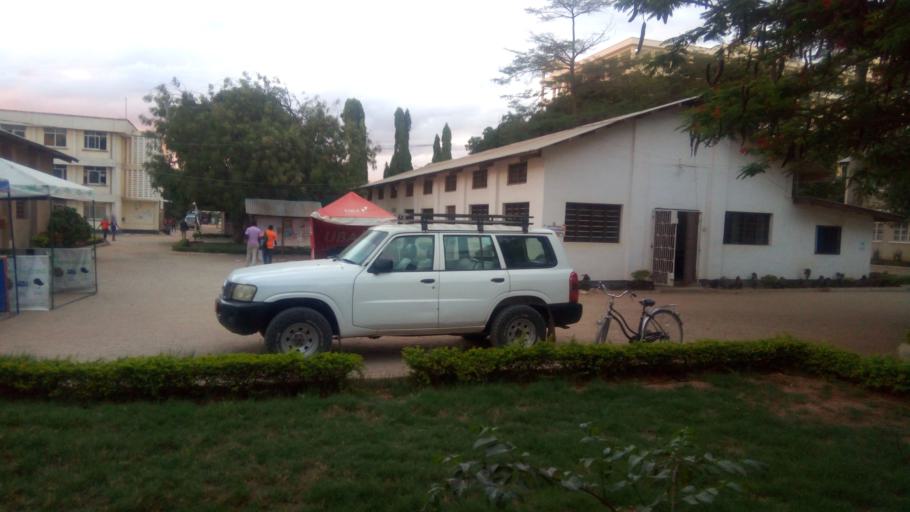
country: TZ
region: Dodoma
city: Dodoma
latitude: -6.1225
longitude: 35.7448
